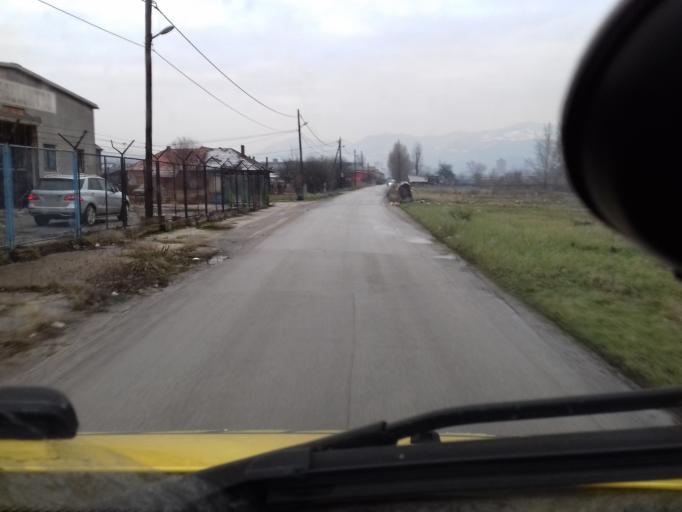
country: BA
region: Federation of Bosnia and Herzegovina
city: Zenica
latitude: 44.2241
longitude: 17.9076
